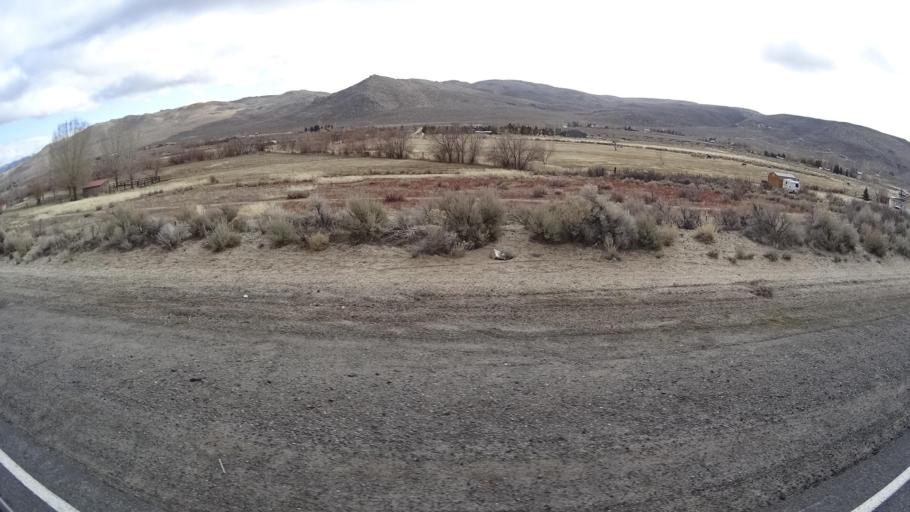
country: US
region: Nevada
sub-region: Washoe County
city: Cold Springs
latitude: 39.8498
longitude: -119.9352
